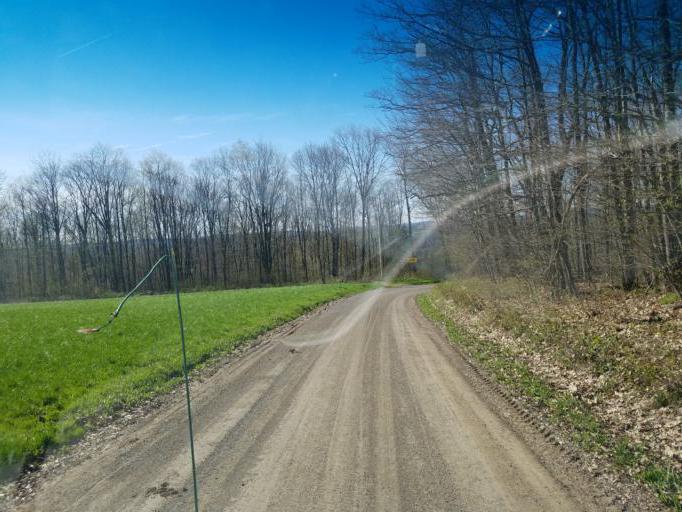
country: US
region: New York
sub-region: Allegany County
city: Andover
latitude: 41.9761
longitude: -77.7856
